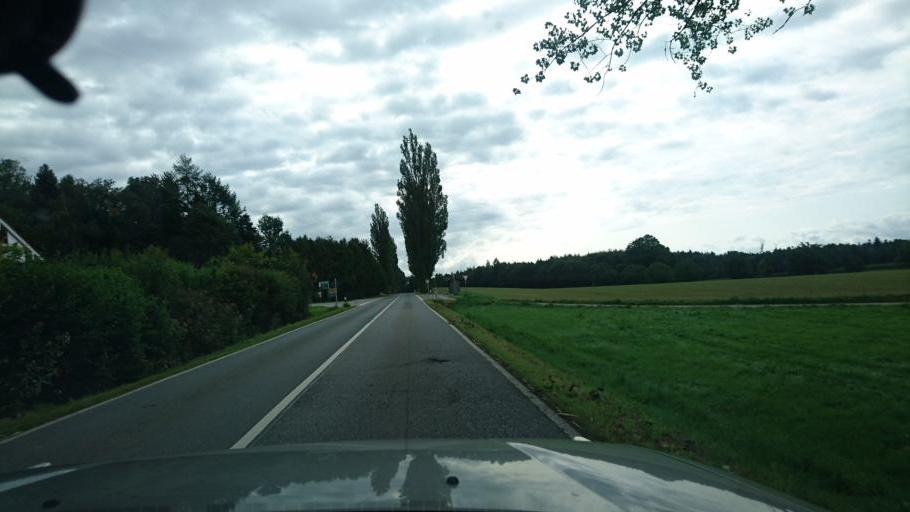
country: DE
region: Bavaria
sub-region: Upper Bavaria
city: Chieming
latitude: 47.9224
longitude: 12.4971
